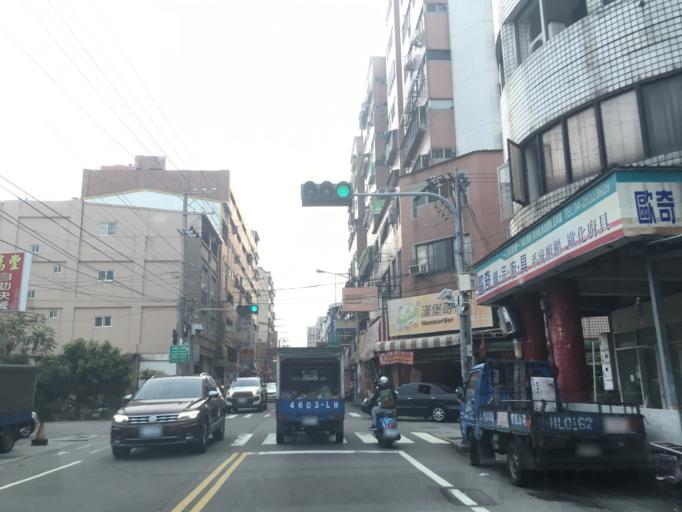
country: TW
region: Taiwan
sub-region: Taichung City
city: Taichung
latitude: 24.1941
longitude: 120.6955
